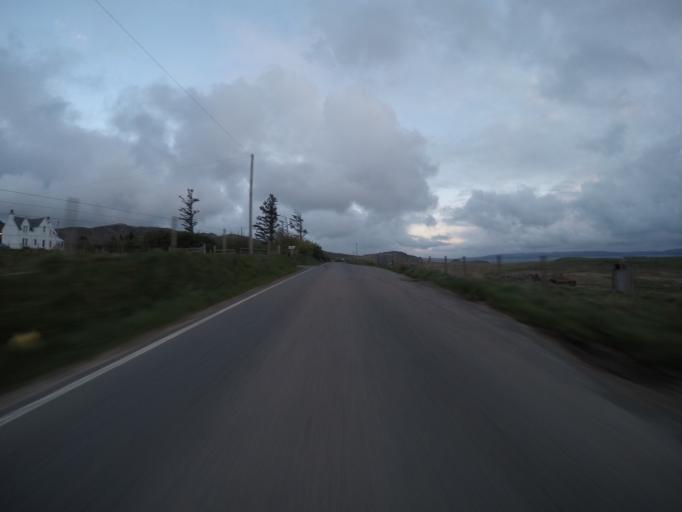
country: GB
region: Scotland
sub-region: Highland
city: Portree
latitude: 57.6270
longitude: -6.3776
